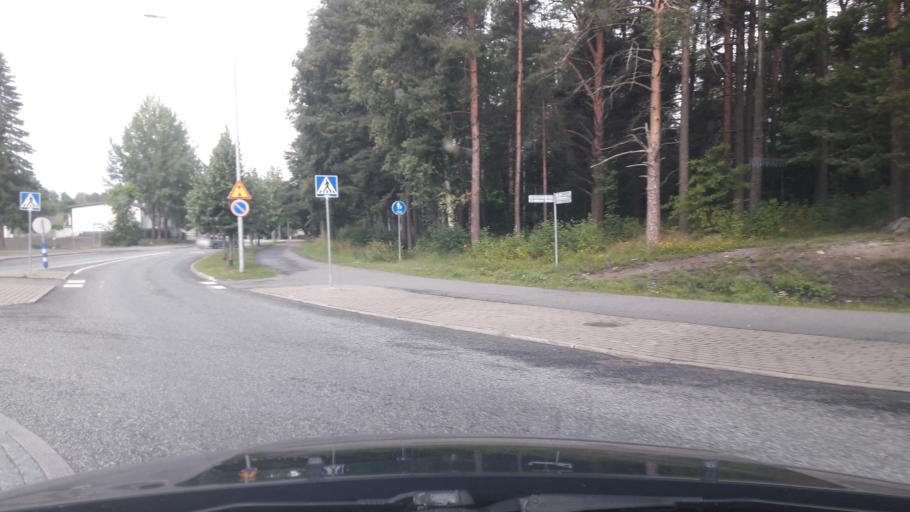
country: FI
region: North Karelia
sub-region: Joensuu
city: Joensuu
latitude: 62.6031
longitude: 29.8039
